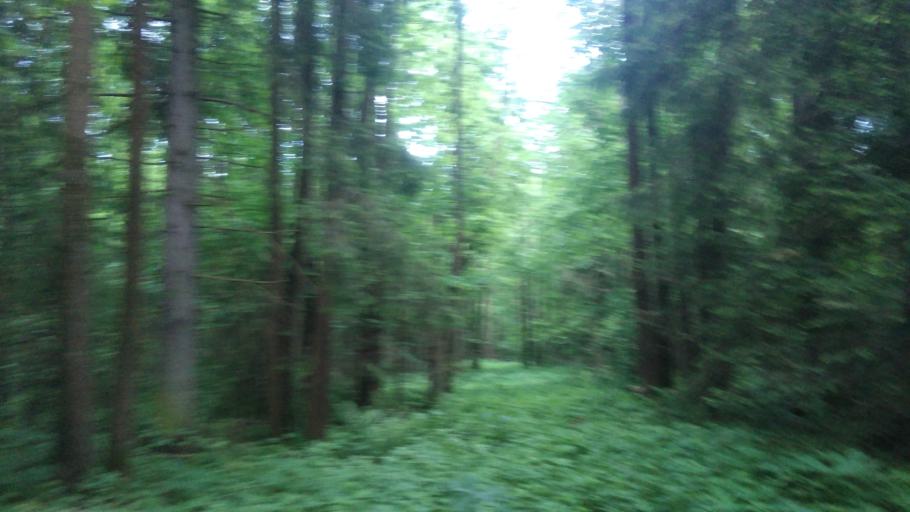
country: RU
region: Perm
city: Ferma
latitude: 57.9638
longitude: 56.3435
